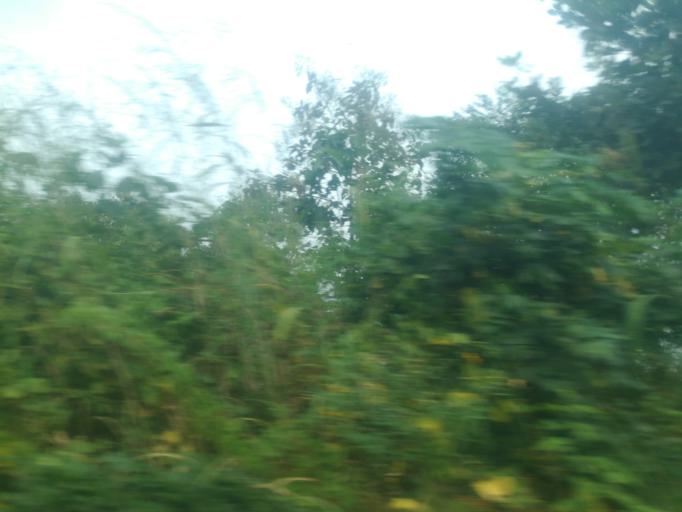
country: NG
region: Ogun
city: Ayetoro
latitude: 7.3509
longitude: 3.0536
